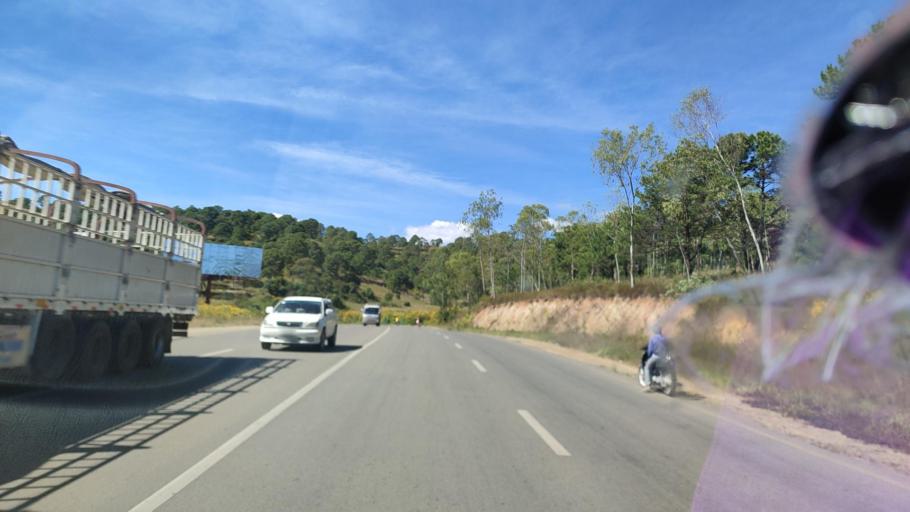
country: MM
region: Shan
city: Taunggyi
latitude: 20.6492
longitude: 96.6172
